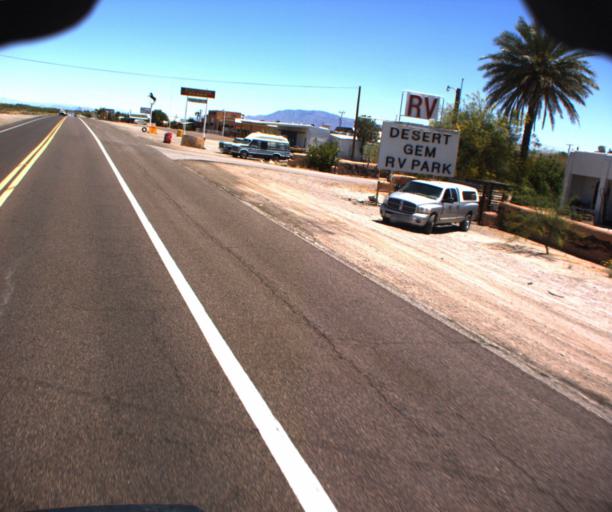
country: US
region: Arizona
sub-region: La Paz County
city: Salome
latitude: 33.7599
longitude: -113.6540
